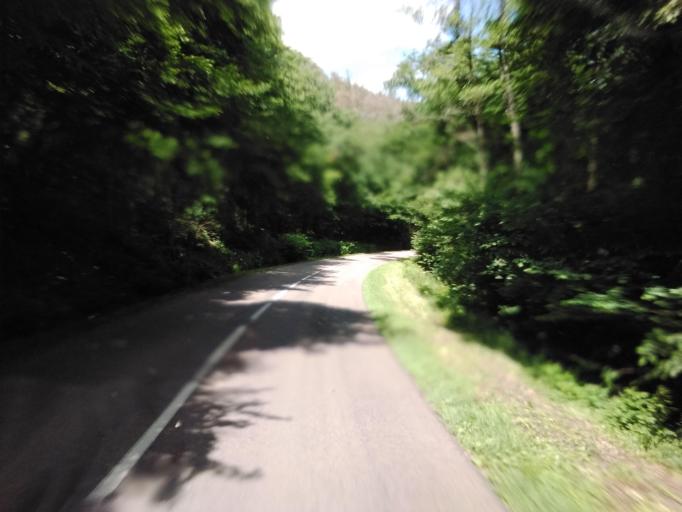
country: FR
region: Bourgogne
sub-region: Departement de l'Yonne
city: Avallon
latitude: 47.4710
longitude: 3.9081
